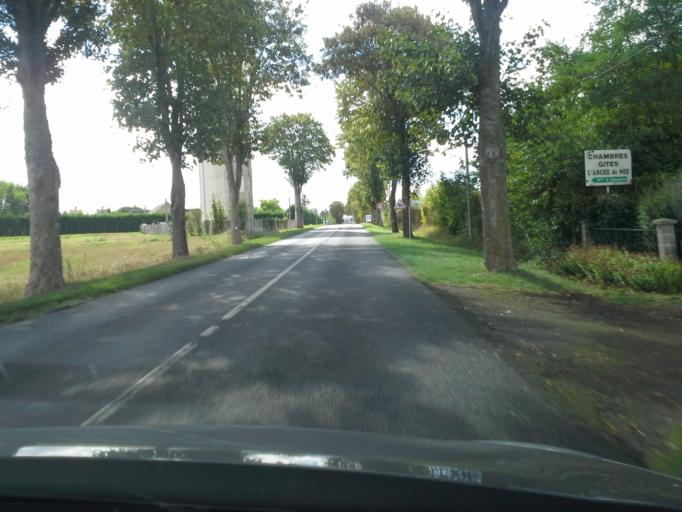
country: FR
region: Centre
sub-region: Departement du Loir-et-Cher
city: Pontlevoy
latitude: 47.3990
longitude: 1.2618
